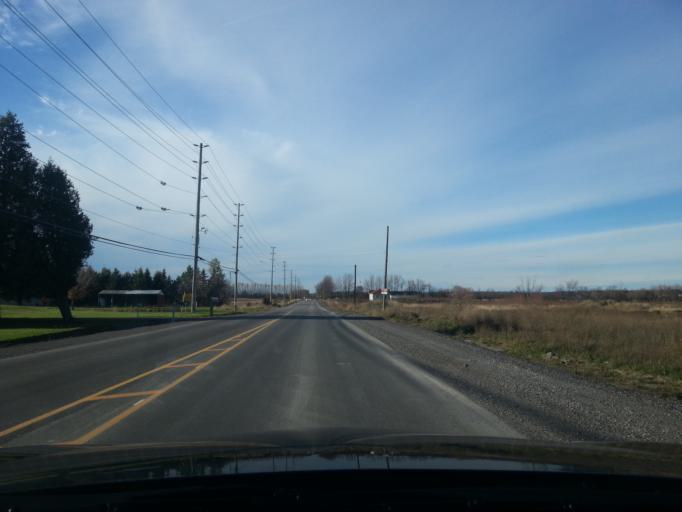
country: CA
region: Ontario
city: Bells Corners
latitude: 45.3033
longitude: -75.9385
